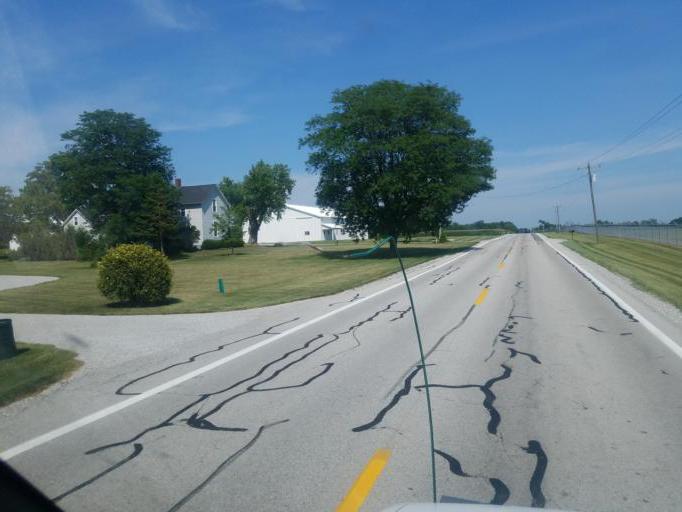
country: US
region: Ohio
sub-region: Auglaize County
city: New Bremen
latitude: 40.4961
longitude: -84.2910
